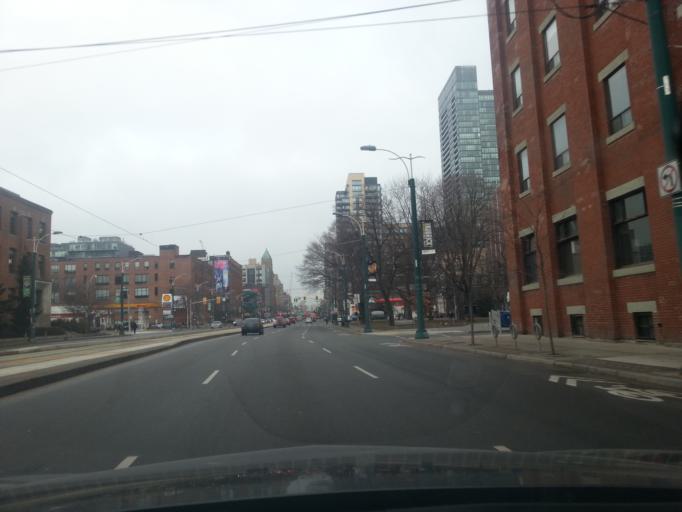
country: CA
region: Ontario
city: Toronto
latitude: 43.6432
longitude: -79.3940
